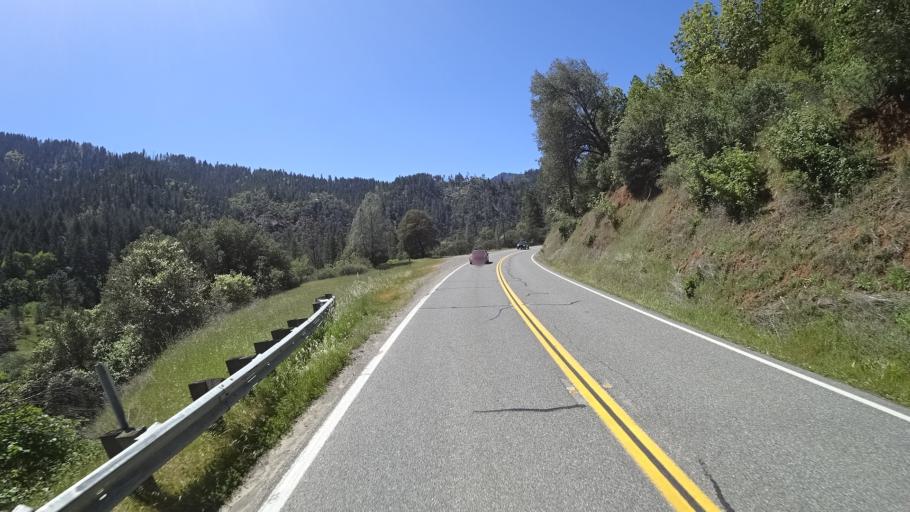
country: US
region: California
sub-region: Trinity County
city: Hayfork
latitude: 40.7738
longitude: -123.3300
